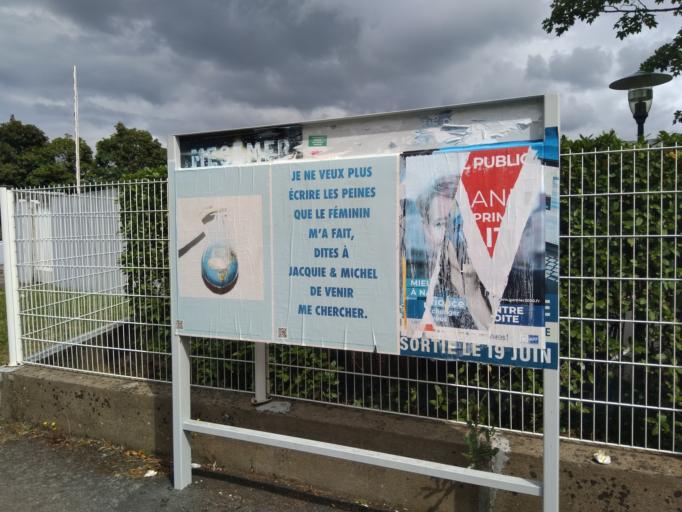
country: FR
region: Pays de la Loire
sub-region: Departement de la Loire-Atlantique
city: Sainte-Luce-sur-Loire
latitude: 47.2564
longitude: -1.5158
